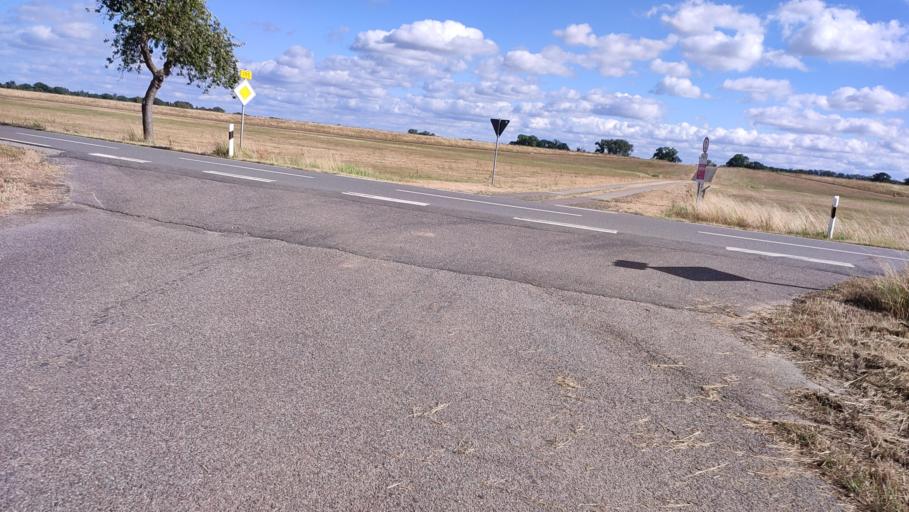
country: DE
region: Lower Saxony
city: Damnatz
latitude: 53.1802
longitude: 11.1475
